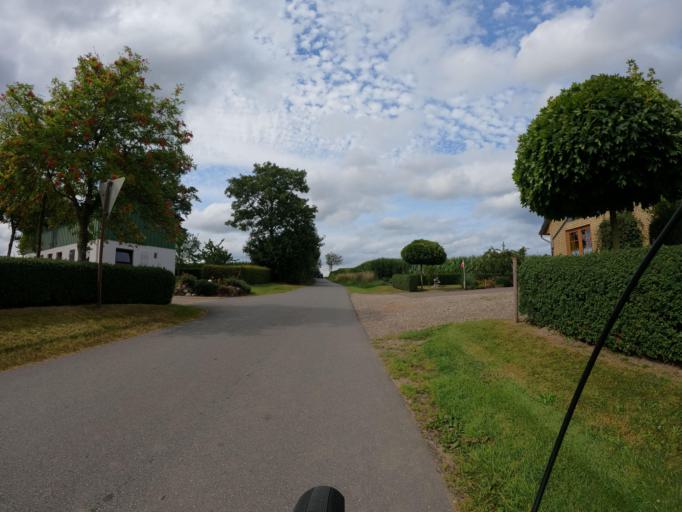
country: DE
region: Schleswig-Holstein
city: Steinberg
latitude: 54.7445
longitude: 9.7835
